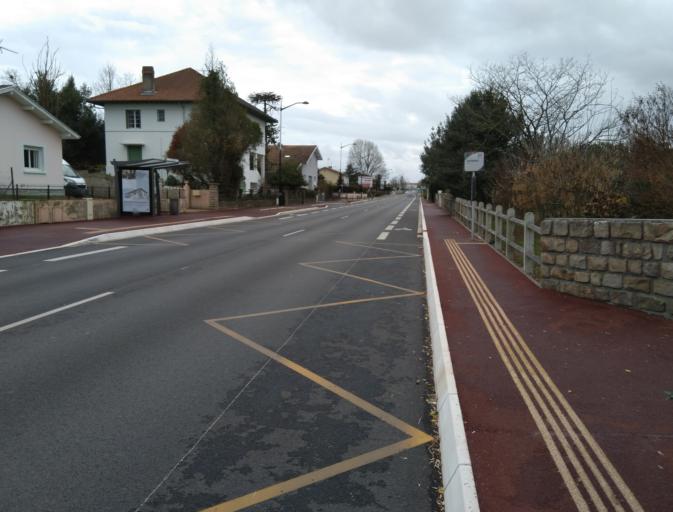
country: FR
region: Aquitaine
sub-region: Departement des Landes
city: Dax
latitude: 43.6958
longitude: -1.0682
